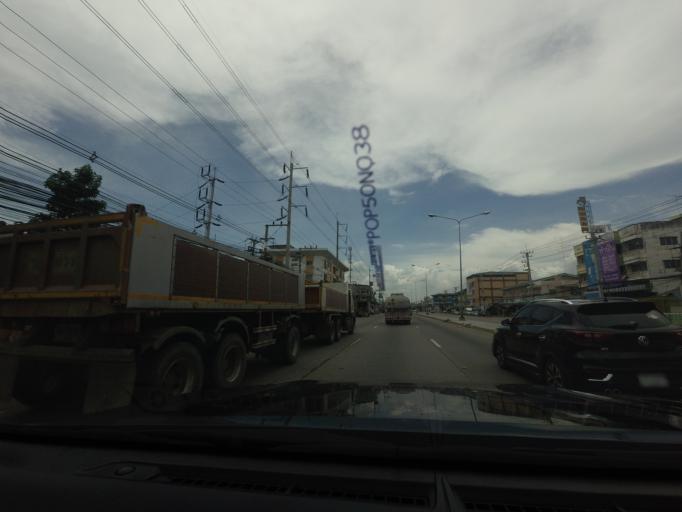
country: TH
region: Nakhon Pathom
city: Nakhon Pathom
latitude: 13.8396
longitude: 100.0289
